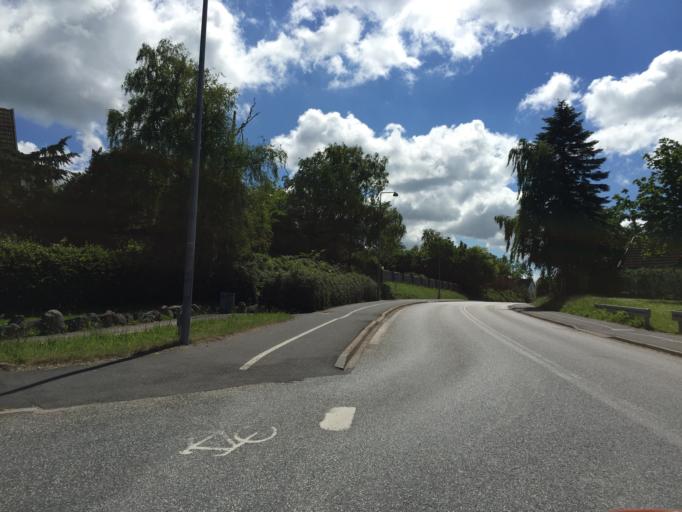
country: DK
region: Zealand
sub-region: Lejre Kommune
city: Norre Hvalso
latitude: 55.6059
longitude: 11.8578
